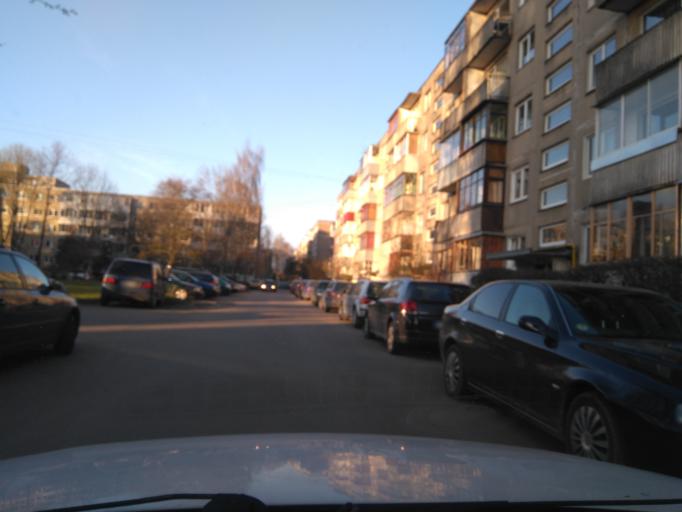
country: LT
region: Kauno apskritis
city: Dainava (Kaunas)
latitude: 54.9213
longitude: 23.9744
